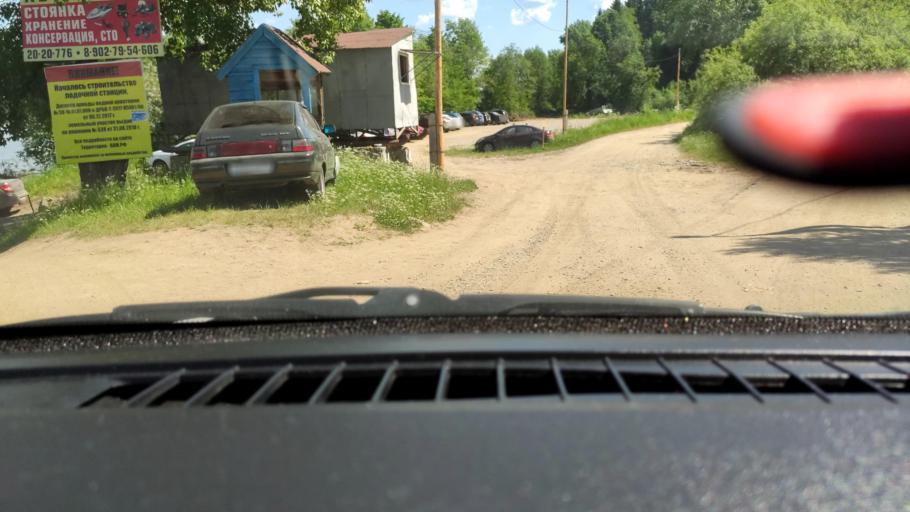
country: RU
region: Perm
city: Sylva
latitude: 58.0371
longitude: 56.7835
